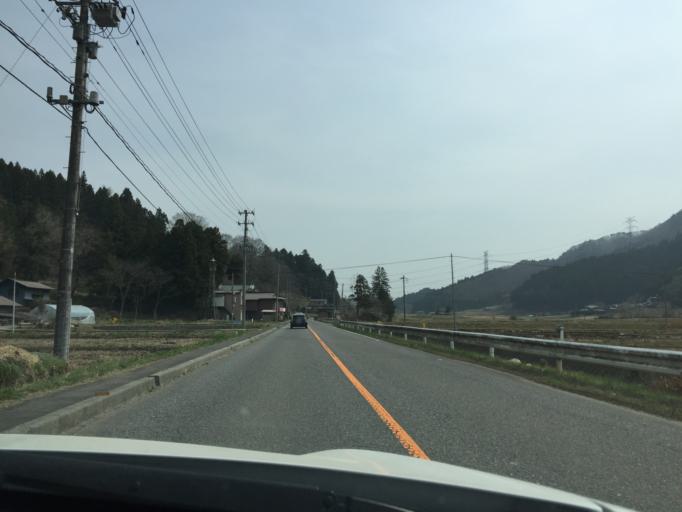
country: JP
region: Fukushima
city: Ishikawa
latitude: 37.1315
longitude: 140.4952
